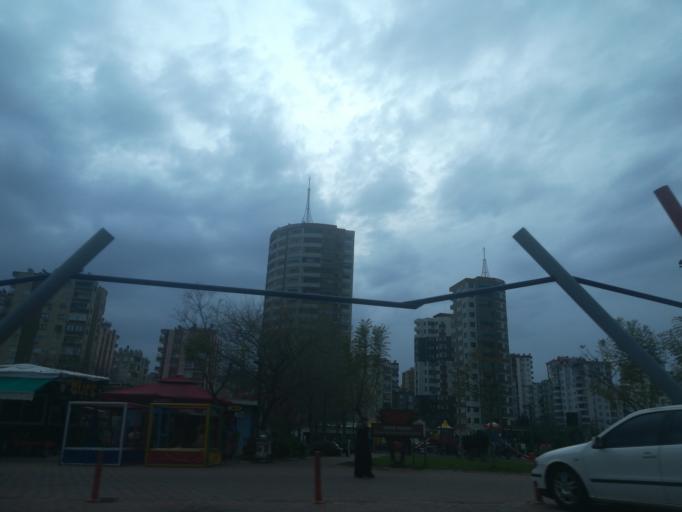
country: TR
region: Adana
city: Adana
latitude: 37.0423
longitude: 35.2916
